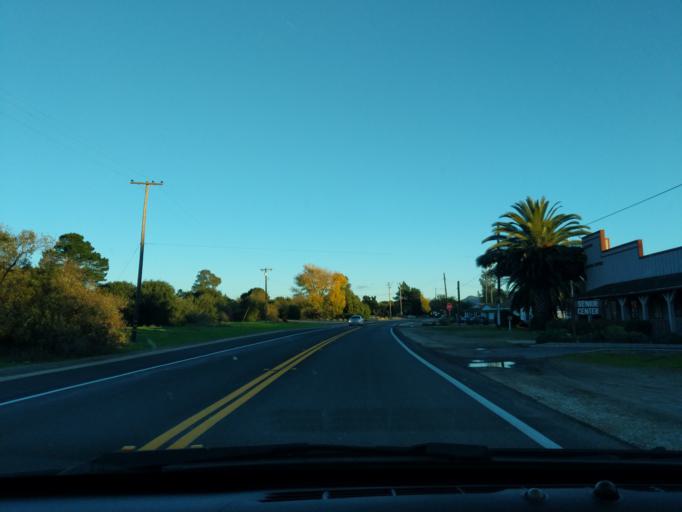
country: US
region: California
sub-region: Santa Barbara County
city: Los Alamos
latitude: 34.7436
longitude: -120.2747
